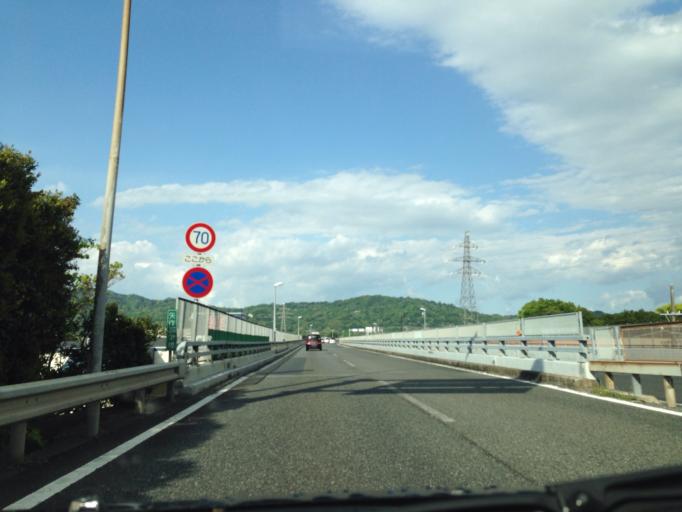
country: JP
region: Kanagawa
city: Odawara
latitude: 35.2889
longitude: 139.1751
